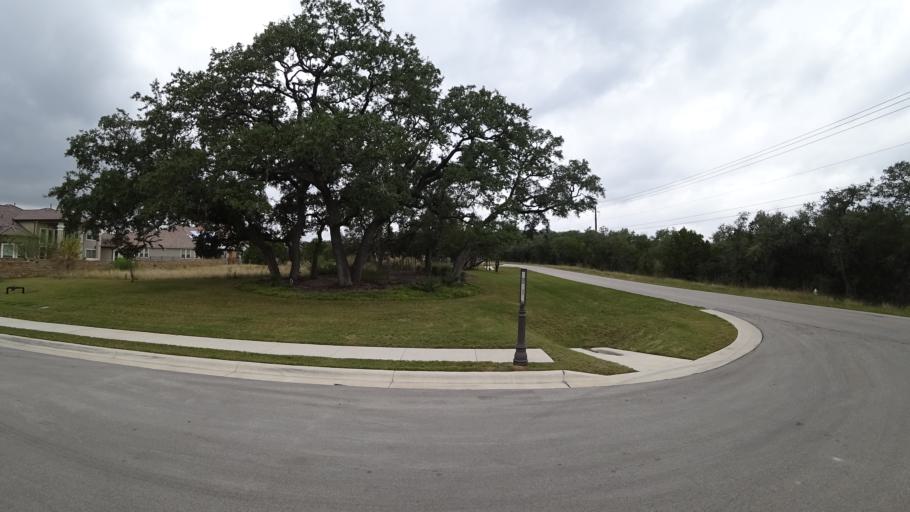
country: US
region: Texas
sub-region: Travis County
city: Bee Cave
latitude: 30.3371
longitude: -97.9147
